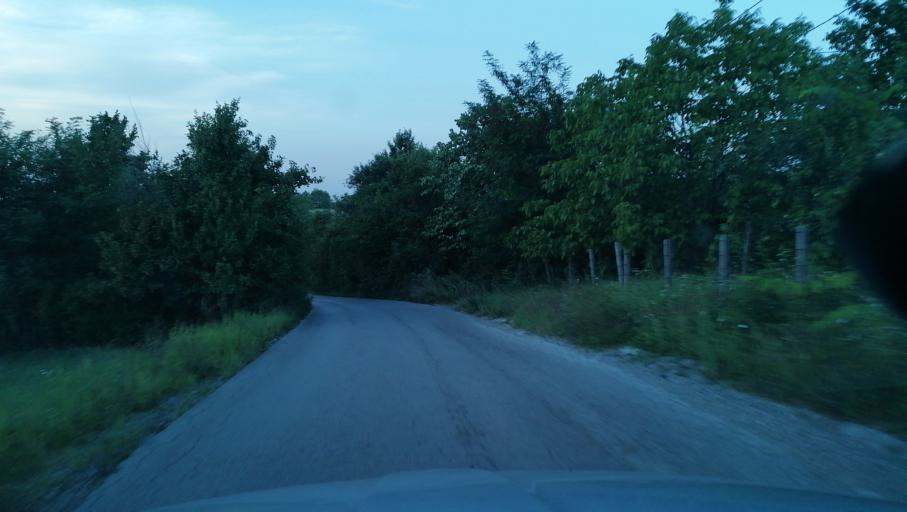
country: RS
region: Central Serbia
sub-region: Kolubarski Okrug
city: Valjevo
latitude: 44.2484
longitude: 19.8728
